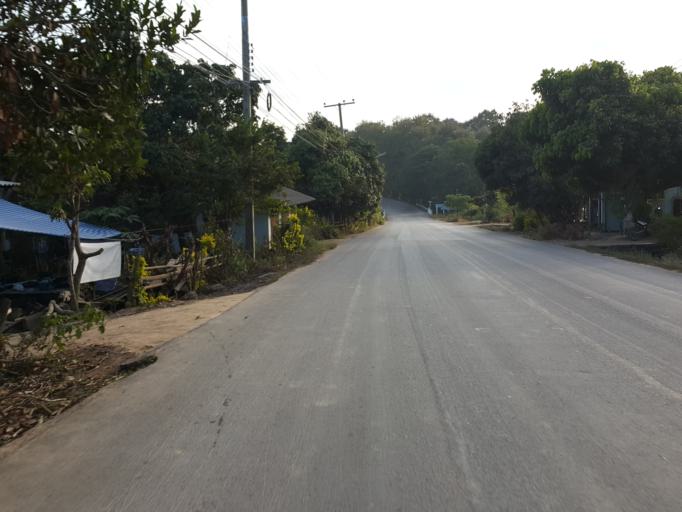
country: TH
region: Lamphun
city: Thung Hua Chang
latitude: 18.0197
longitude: 99.0274
